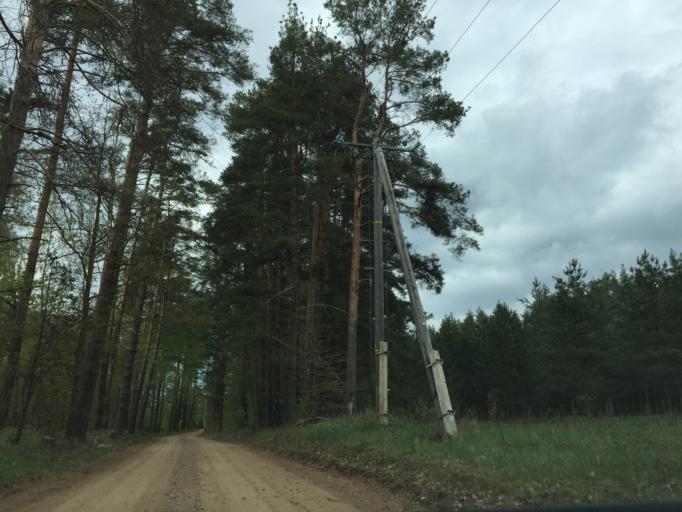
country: LV
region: Kekava
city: Kekava
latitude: 56.7949
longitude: 24.3084
